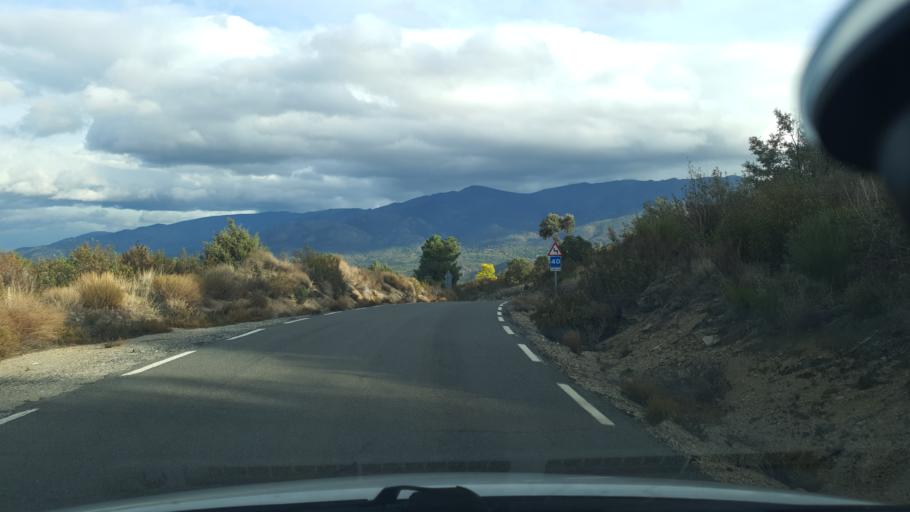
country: ES
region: Castille and Leon
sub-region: Provincia de Avila
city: Burgohondo
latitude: 40.4110
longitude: -4.8261
